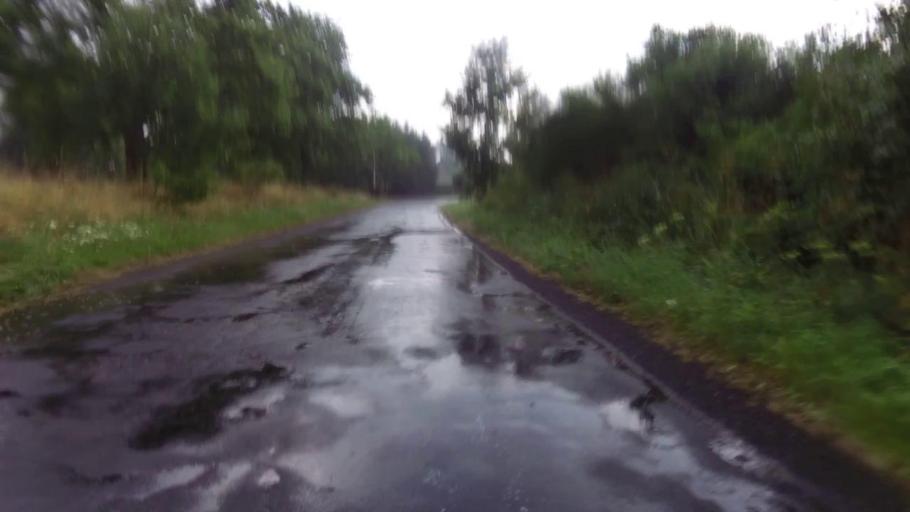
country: PL
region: West Pomeranian Voivodeship
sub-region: Powiat choszczenski
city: Recz
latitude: 53.2790
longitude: 15.4636
